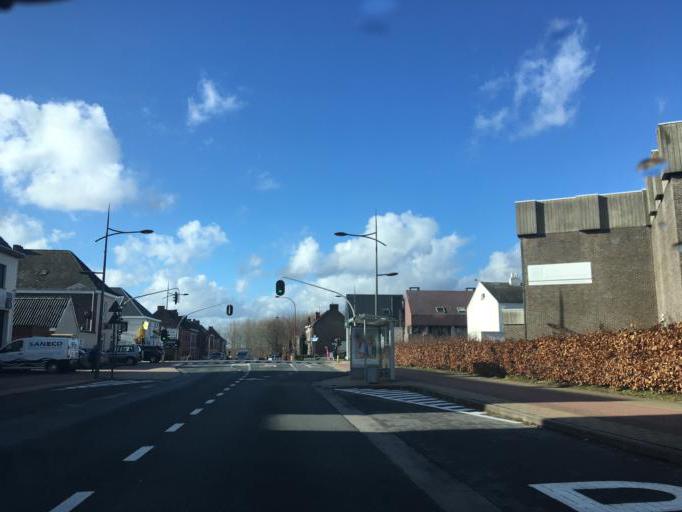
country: BE
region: Flanders
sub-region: Provincie Oost-Vlaanderen
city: Merelbeke
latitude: 50.9976
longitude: 3.7433
